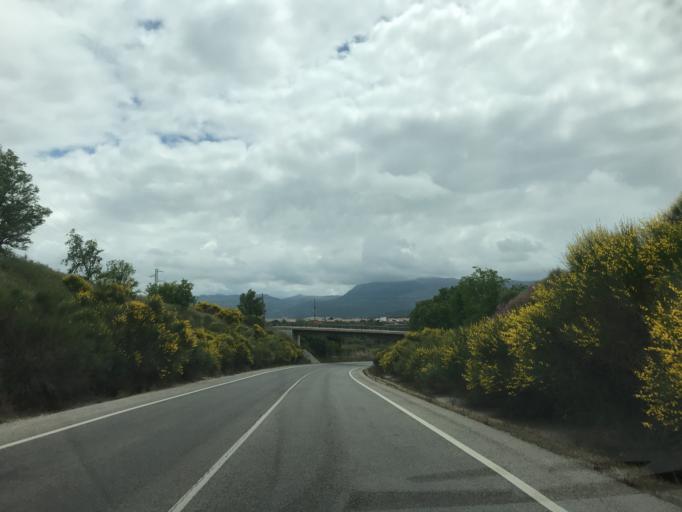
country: ES
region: Andalusia
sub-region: Provincia de Malaga
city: Ronda
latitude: 36.7253
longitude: -5.1664
